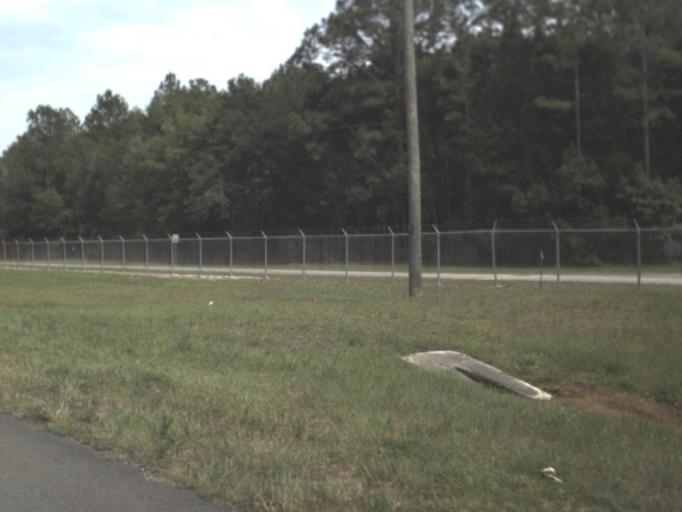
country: US
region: Florida
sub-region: Duval County
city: Baldwin
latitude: 30.2464
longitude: -81.8661
